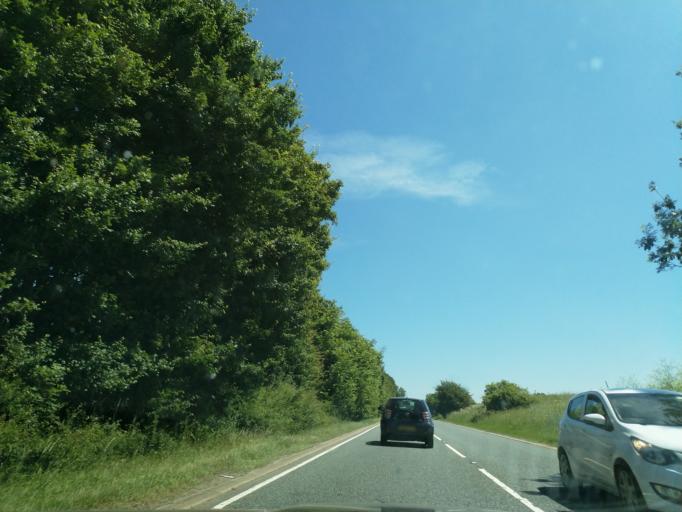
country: GB
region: England
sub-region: Warwickshire
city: Warwick
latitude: 52.2570
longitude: -1.5782
